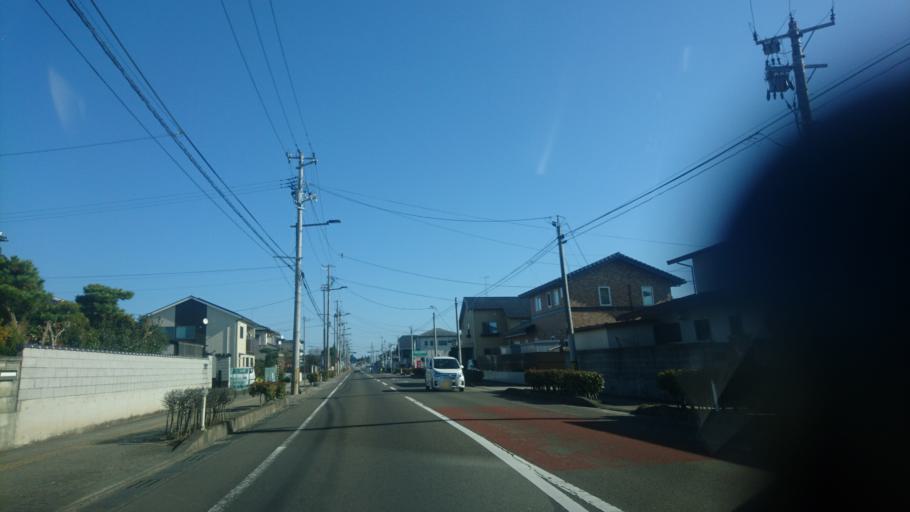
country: JP
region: Miyagi
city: Iwanuma
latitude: 38.1158
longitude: 140.8706
